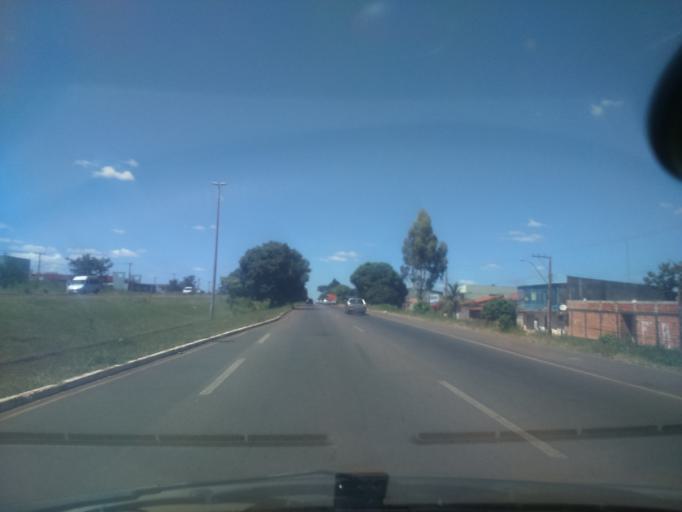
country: BR
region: Goias
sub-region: Luziania
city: Luziania
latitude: -16.0492
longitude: -47.9963
